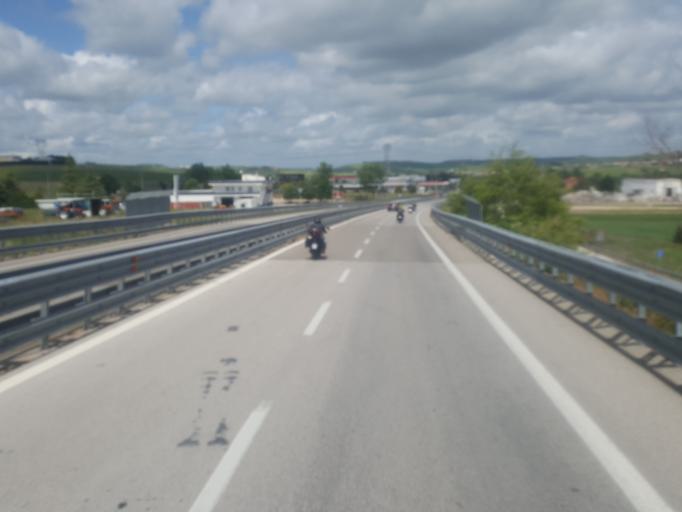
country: IT
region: Basilicate
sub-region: Provincia di Matera
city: Matera
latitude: 40.7069
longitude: 16.5825
